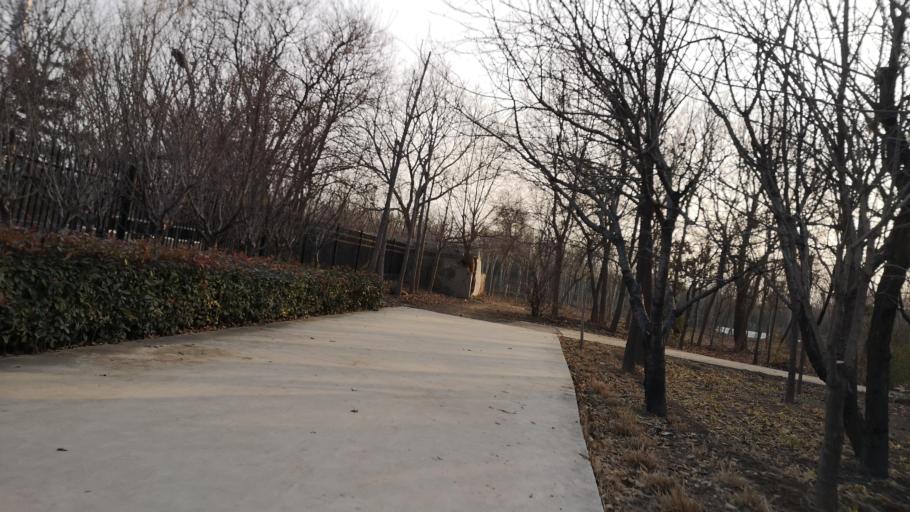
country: CN
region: Henan Sheng
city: Zhongyuanlu
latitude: 35.7422
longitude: 115.0637
